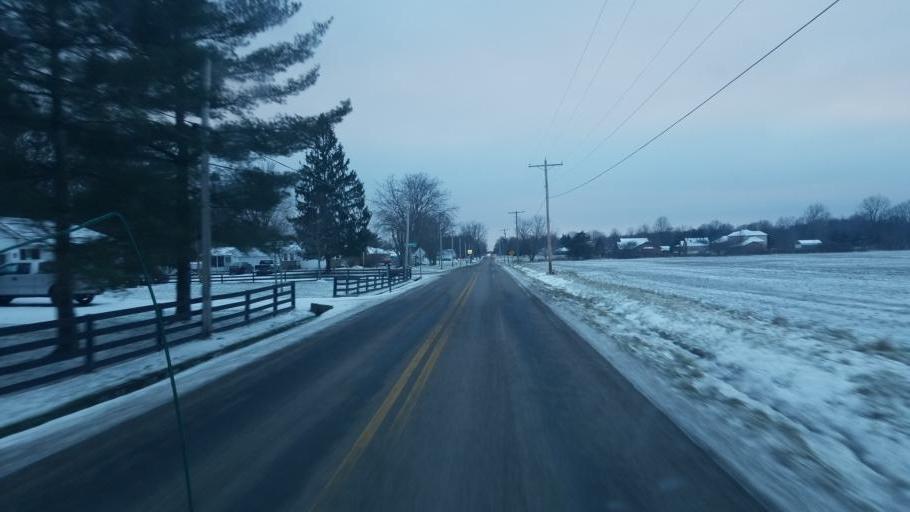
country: US
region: Ohio
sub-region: Franklin County
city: New Albany
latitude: 40.1524
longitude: -82.8421
